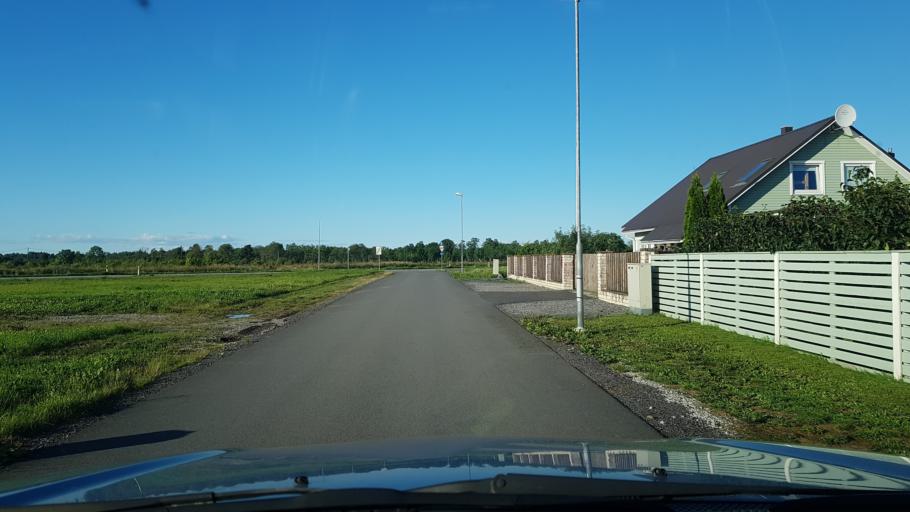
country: EE
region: Harju
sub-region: Rae vald
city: Jueri
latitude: 59.3861
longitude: 24.8473
